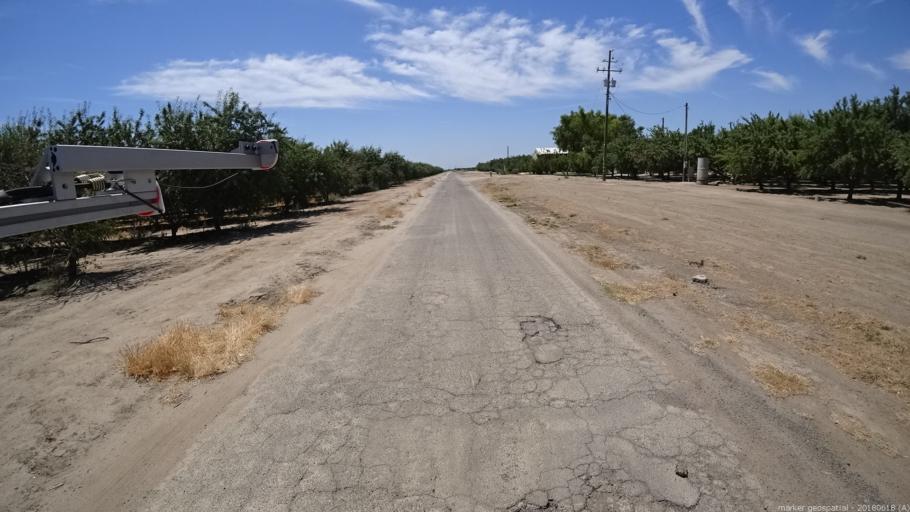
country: US
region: California
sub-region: Madera County
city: Parkwood
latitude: 36.8758
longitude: -120.1013
